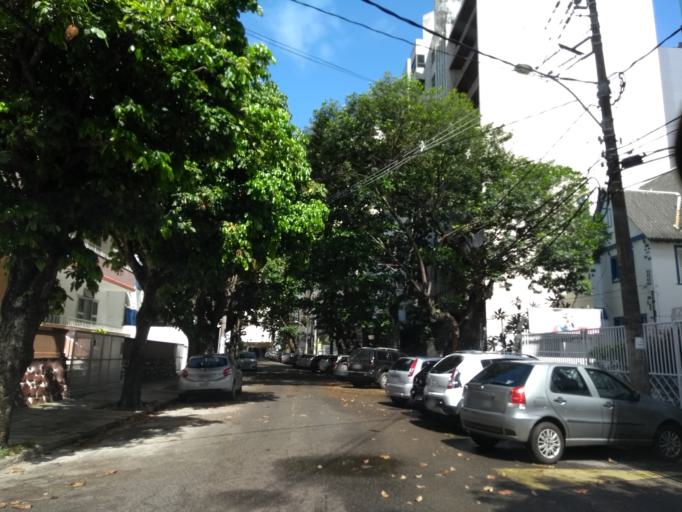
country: BR
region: Bahia
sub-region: Salvador
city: Salvador
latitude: -13.0051
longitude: -38.5274
